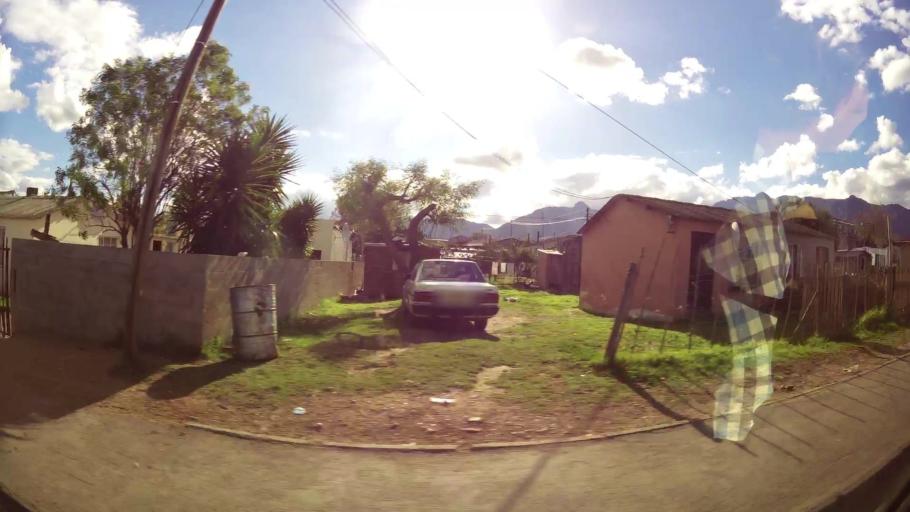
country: ZA
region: Western Cape
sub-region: Overberg District Municipality
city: Swellendam
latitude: -34.0379
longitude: 20.4417
